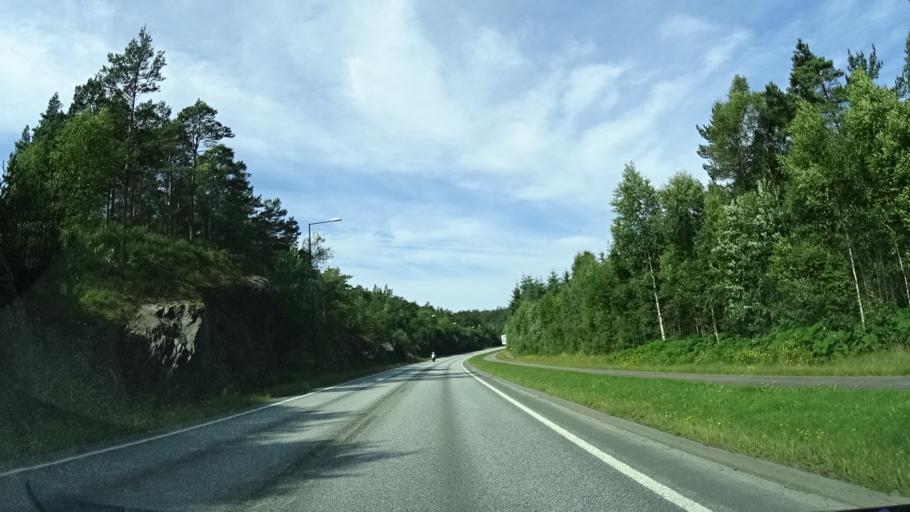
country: NO
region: Hordaland
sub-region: Stord
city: Sagvag
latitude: 59.7607
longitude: 5.4287
